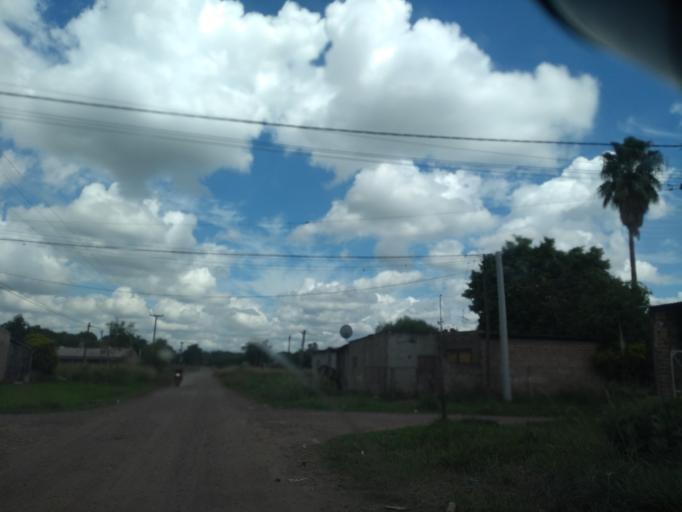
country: AR
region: Chaco
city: Fontana
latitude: -27.4080
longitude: -59.0430
